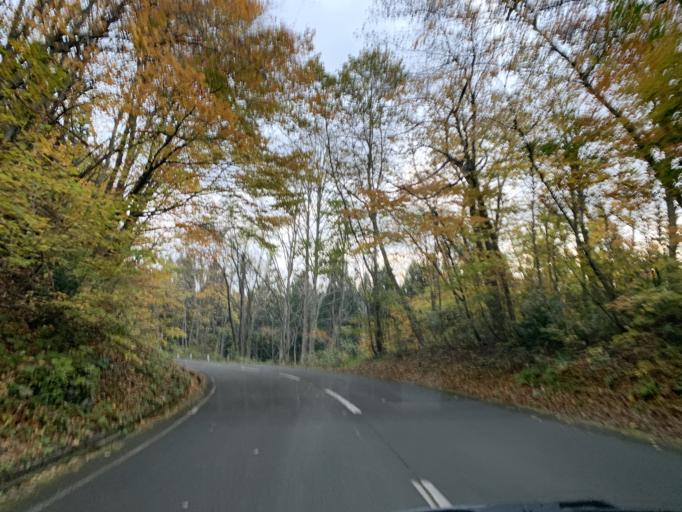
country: JP
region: Iwate
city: Mizusawa
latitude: 39.1077
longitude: 140.8736
